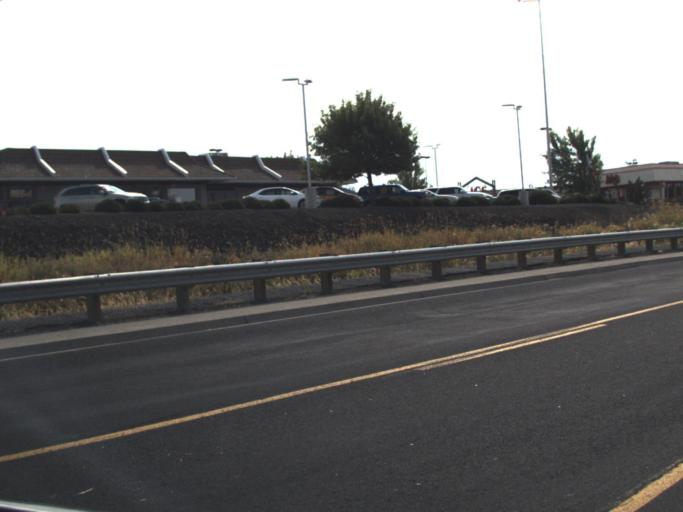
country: US
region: Washington
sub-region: Whitman County
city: Pullman
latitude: 46.7150
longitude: -117.1824
